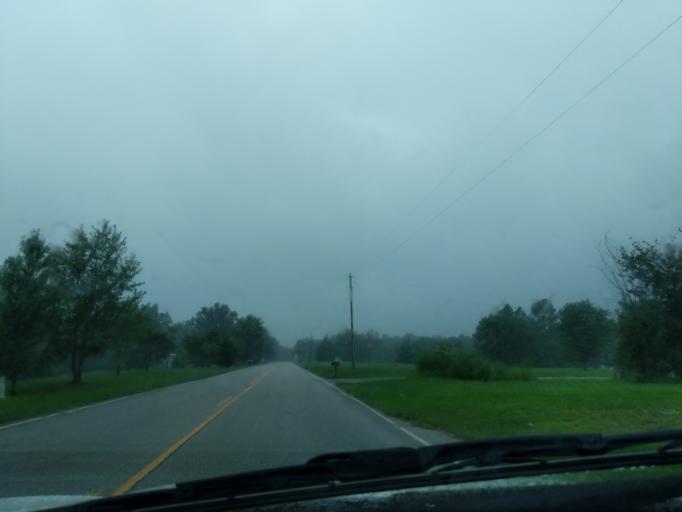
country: US
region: Kentucky
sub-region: Barren County
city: Cave City
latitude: 37.1294
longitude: -86.0504
